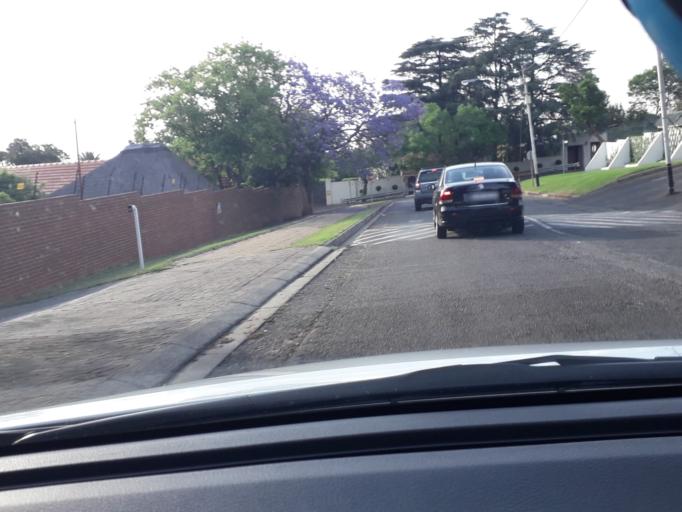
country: ZA
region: Gauteng
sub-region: City of Johannesburg Metropolitan Municipality
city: Johannesburg
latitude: -26.1281
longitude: 27.9909
